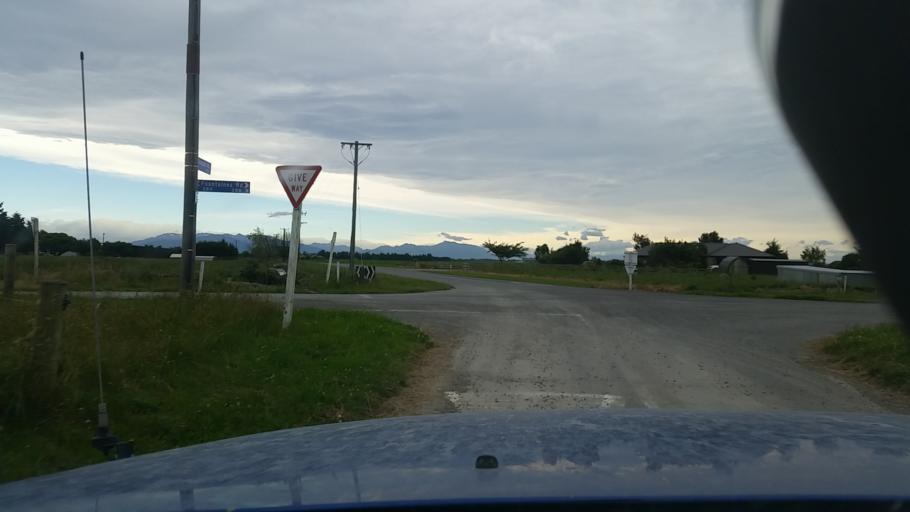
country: NZ
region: Canterbury
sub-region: Ashburton District
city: Tinwald
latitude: -43.9760
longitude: 171.5084
